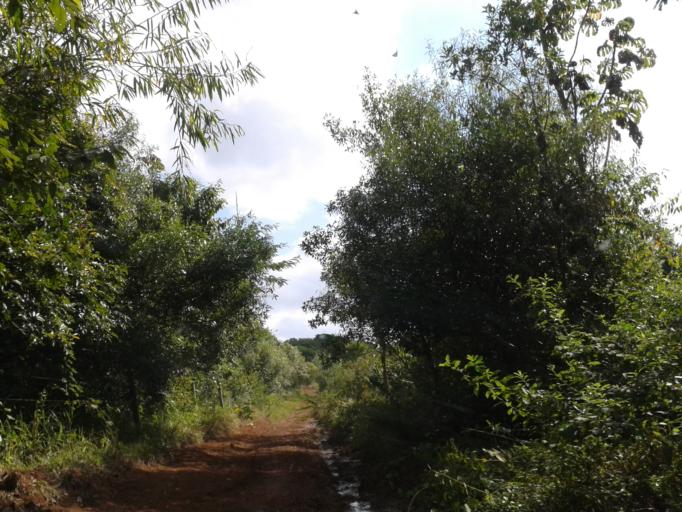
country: BR
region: Minas Gerais
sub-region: Campina Verde
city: Campina Verde
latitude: -19.3940
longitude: -49.6746
